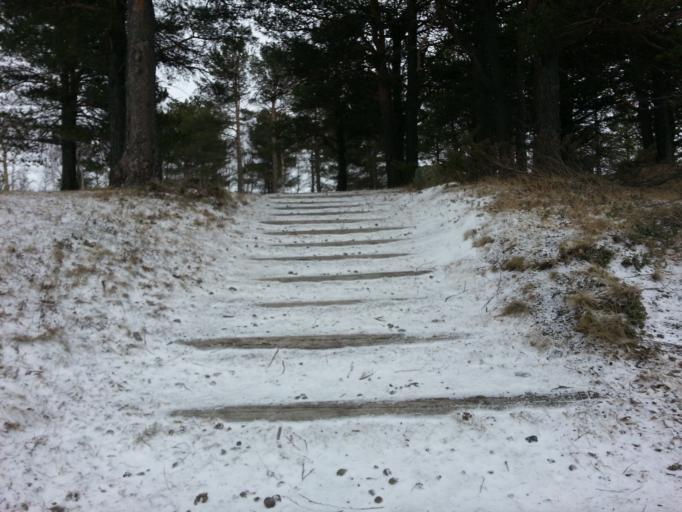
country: NO
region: Sor-Trondelag
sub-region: Oppdal
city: Oppdal
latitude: 62.5951
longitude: 9.6954
